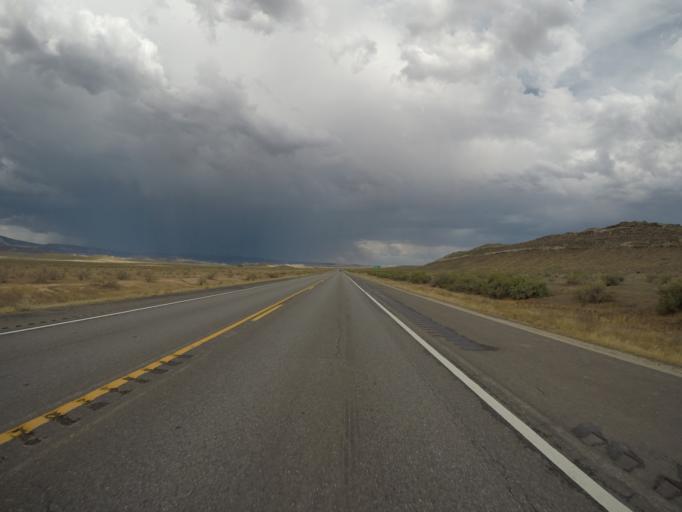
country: US
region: Utah
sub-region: Uintah County
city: Naples
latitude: 40.2899
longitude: -109.1591
